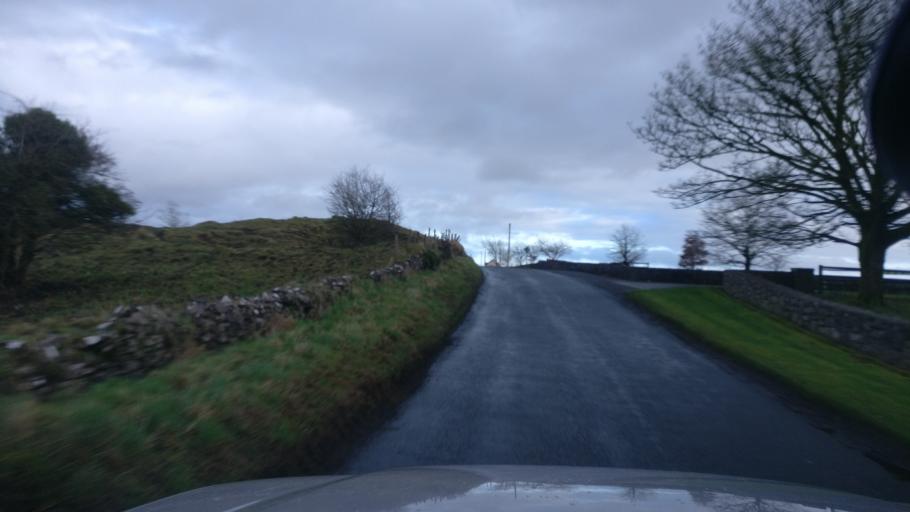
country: IE
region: Connaught
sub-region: County Galway
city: Athenry
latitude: 53.2955
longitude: -8.6959
